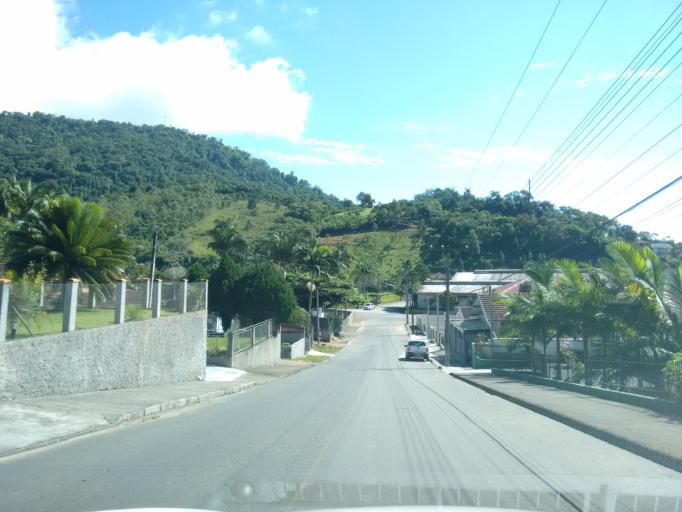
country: BR
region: Santa Catarina
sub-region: Pomerode
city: Pomerode
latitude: -26.7526
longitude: -49.1818
